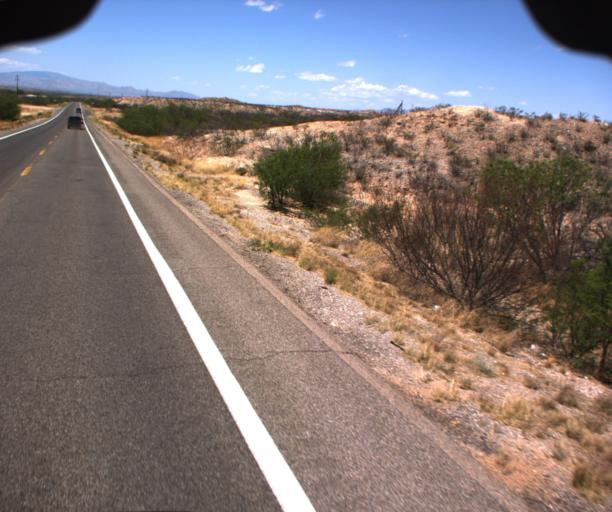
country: US
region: Arizona
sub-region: Cochise County
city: Saint David
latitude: 31.8321
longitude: -110.1822
